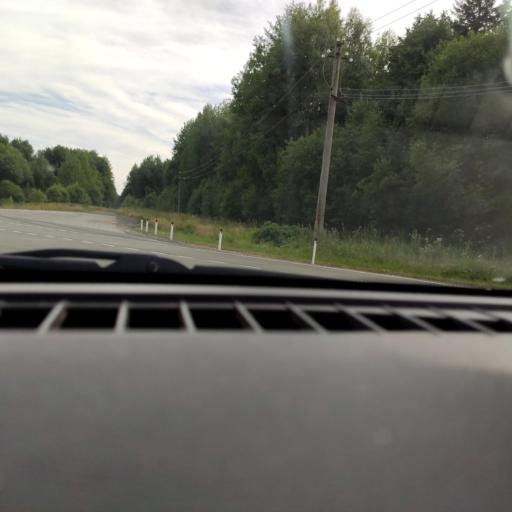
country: RU
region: Perm
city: Polazna
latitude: 58.3150
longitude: 56.1486
